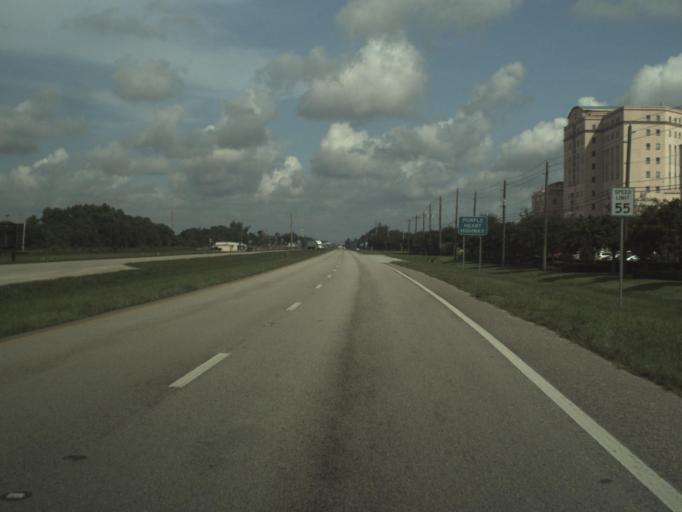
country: US
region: Florida
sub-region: Palm Beach County
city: Mangonia Park
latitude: 26.7814
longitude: -80.1095
